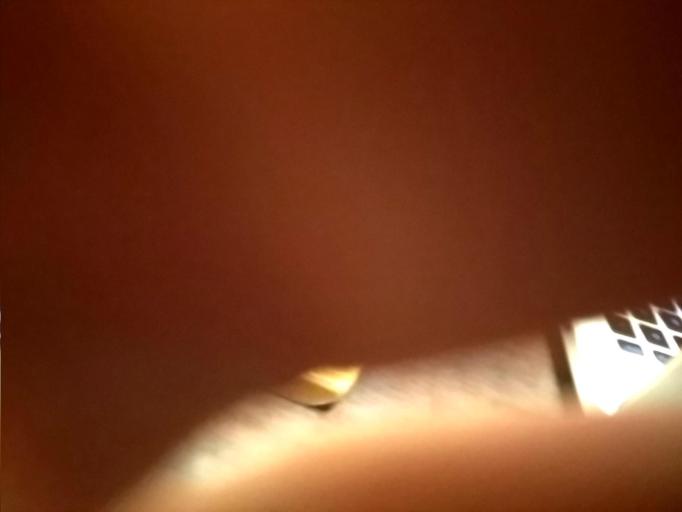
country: RU
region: Moskovskaya
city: Balashikha
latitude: 55.8109
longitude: 37.9637
